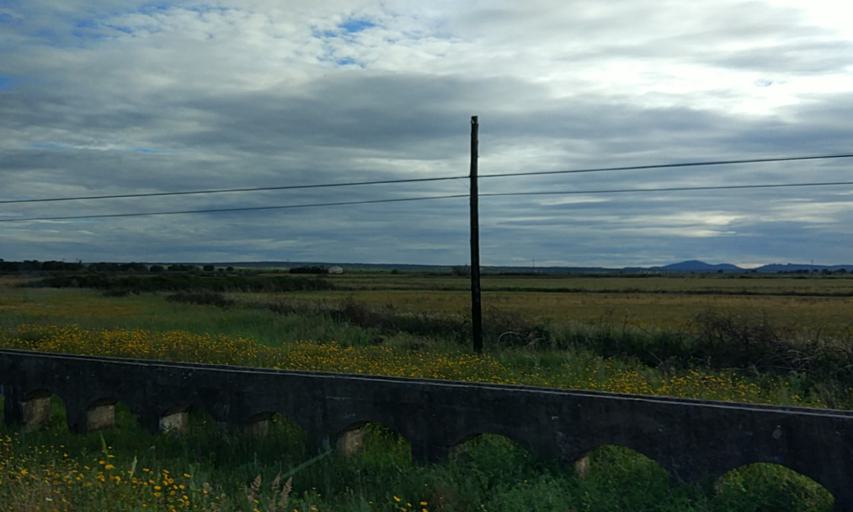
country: ES
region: Extremadura
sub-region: Provincia de Caceres
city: Huelaga
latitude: 40.0445
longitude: -6.6341
